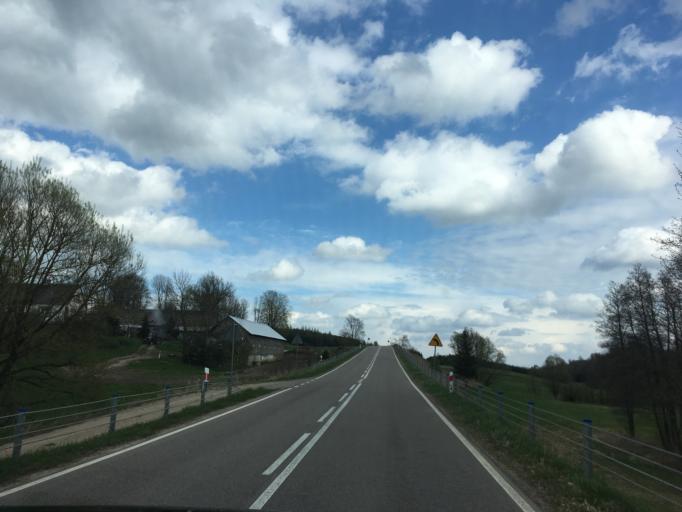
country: PL
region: Podlasie
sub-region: Powiat suwalski
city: Filipow
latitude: 54.3597
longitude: 22.8074
